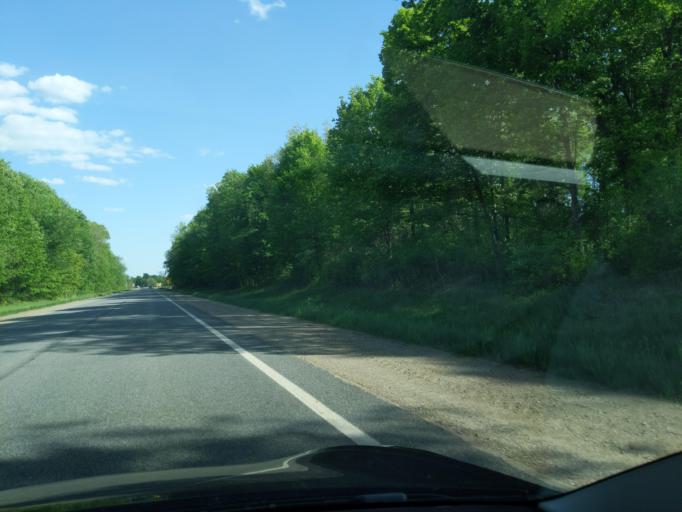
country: US
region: Michigan
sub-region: Eaton County
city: Grand Ledge
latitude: 42.7491
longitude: -84.7648
